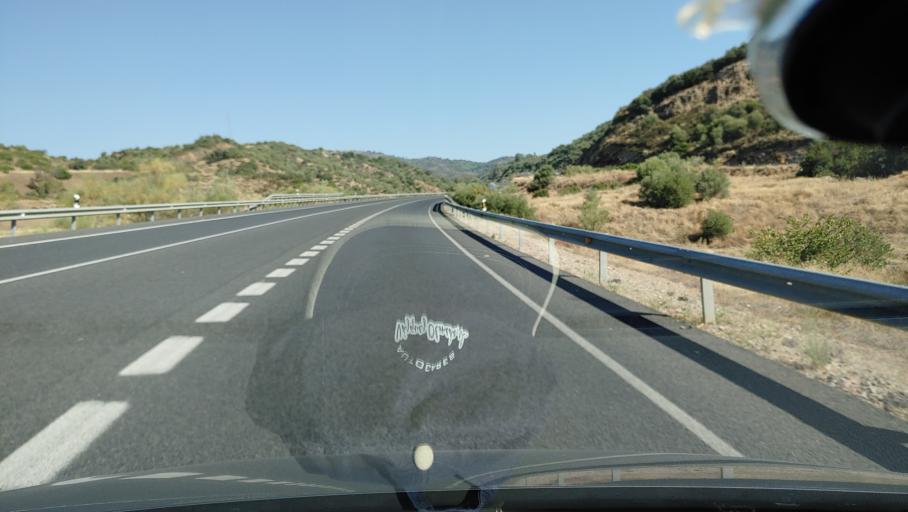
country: ES
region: Andalusia
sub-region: Province of Cordoba
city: Cordoba
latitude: 37.9470
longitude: -4.7647
